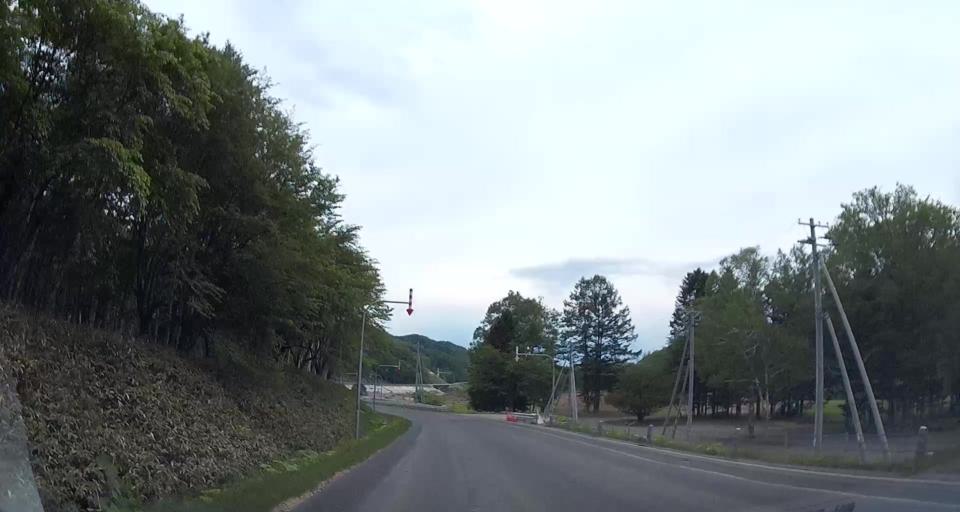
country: JP
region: Hokkaido
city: Chitose
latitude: 42.7925
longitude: 142.0318
